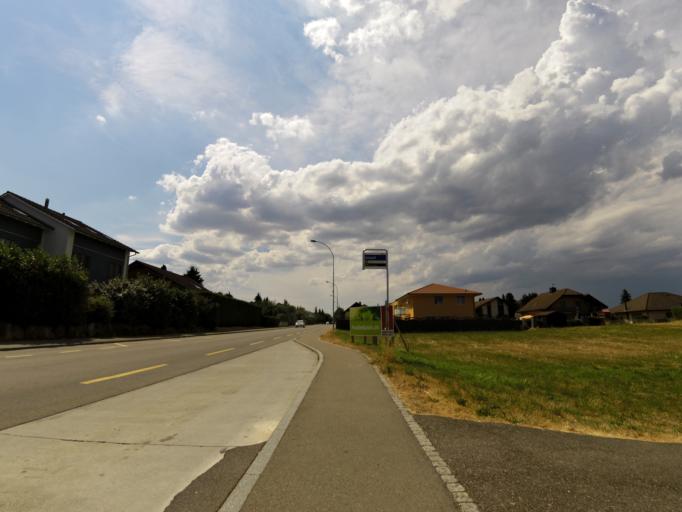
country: CH
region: Aargau
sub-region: Bezirk Lenzburg
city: Othmarsingen
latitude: 47.4120
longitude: 8.2400
